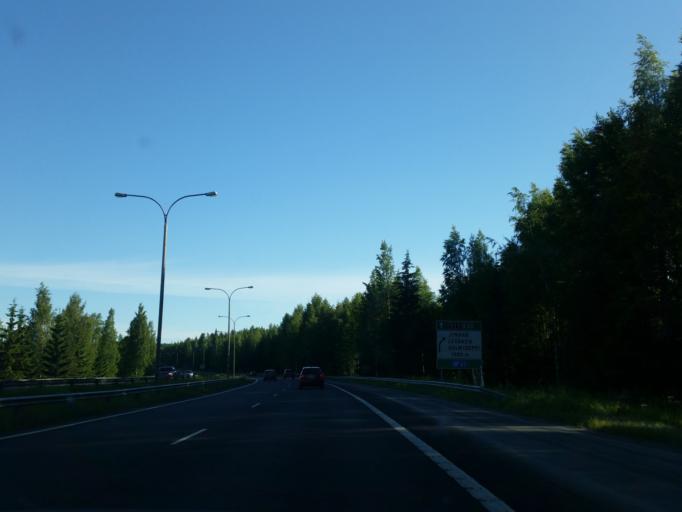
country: FI
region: Northern Savo
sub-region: Kuopio
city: Kuopio
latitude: 62.8759
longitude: 27.6230
